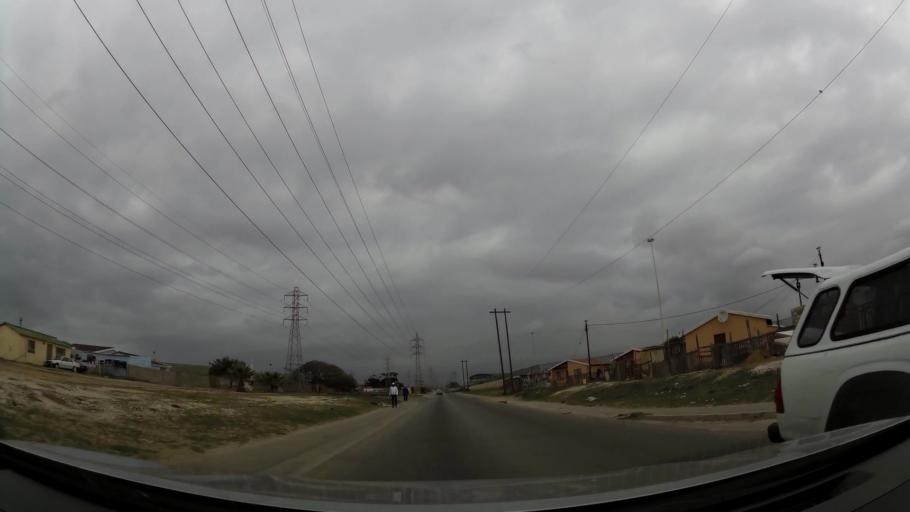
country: ZA
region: Eastern Cape
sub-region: Nelson Mandela Bay Metropolitan Municipality
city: Port Elizabeth
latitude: -33.8763
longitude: 25.5853
